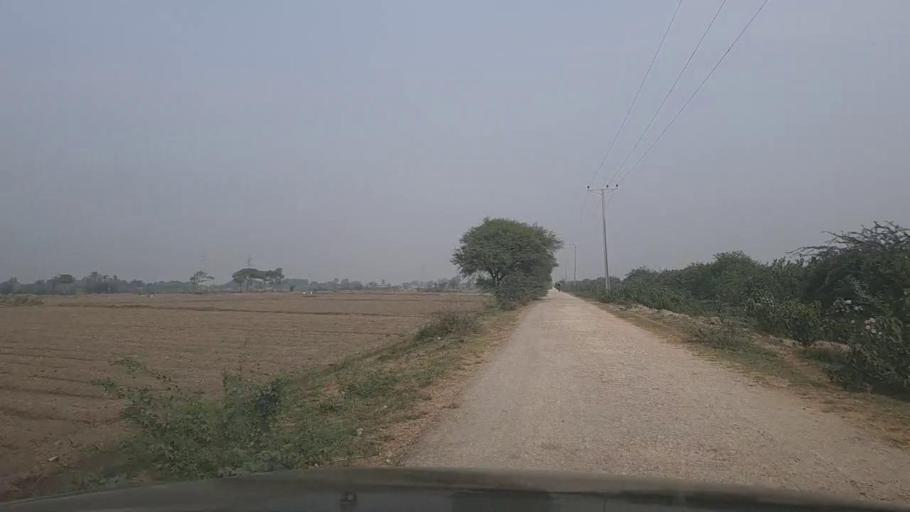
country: PK
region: Sindh
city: Mirpur Sakro
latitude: 24.5666
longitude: 67.7859
